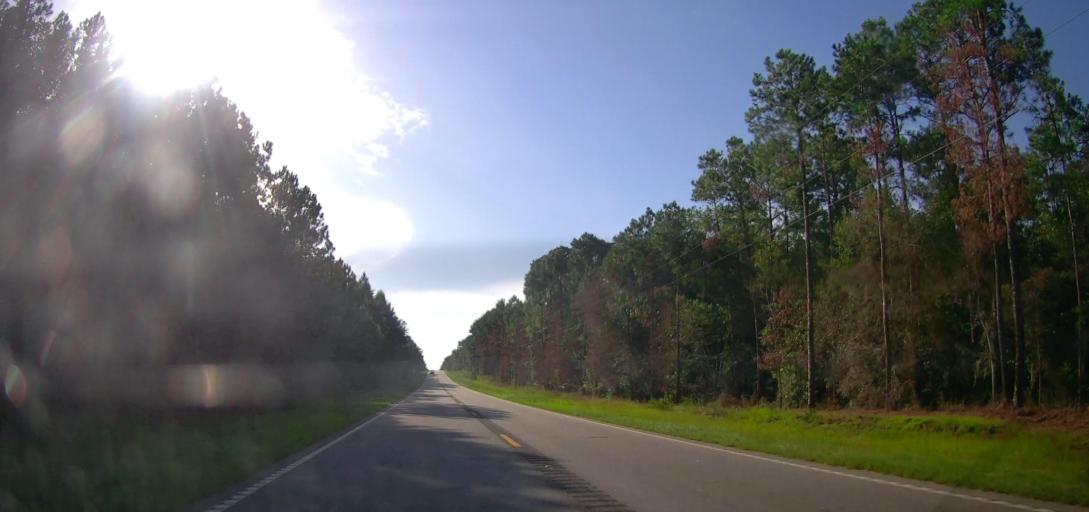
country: US
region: Georgia
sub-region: Coffee County
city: Douglas
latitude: 31.4702
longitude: -82.7702
